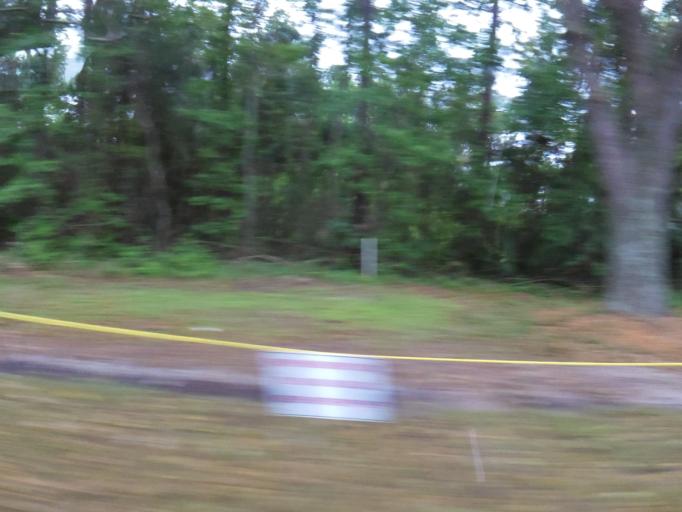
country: US
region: Florida
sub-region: Nassau County
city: Nassau Village-Ratliff
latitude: 30.4884
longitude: -81.6795
